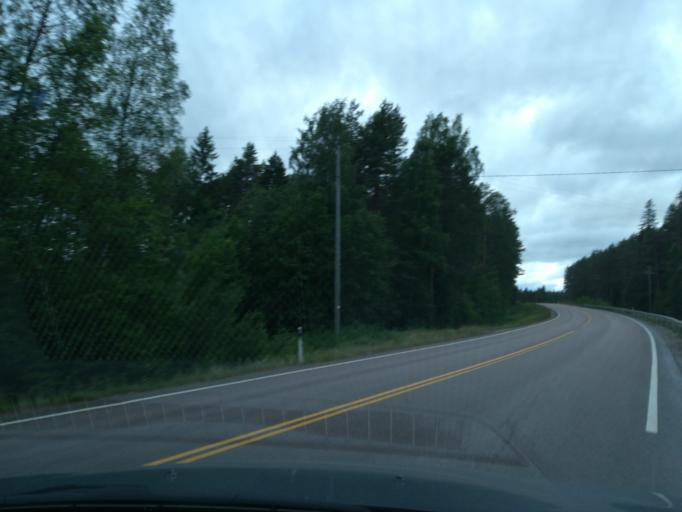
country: FI
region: Southern Savonia
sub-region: Mikkeli
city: Ristiina
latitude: 61.2753
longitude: 27.4071
